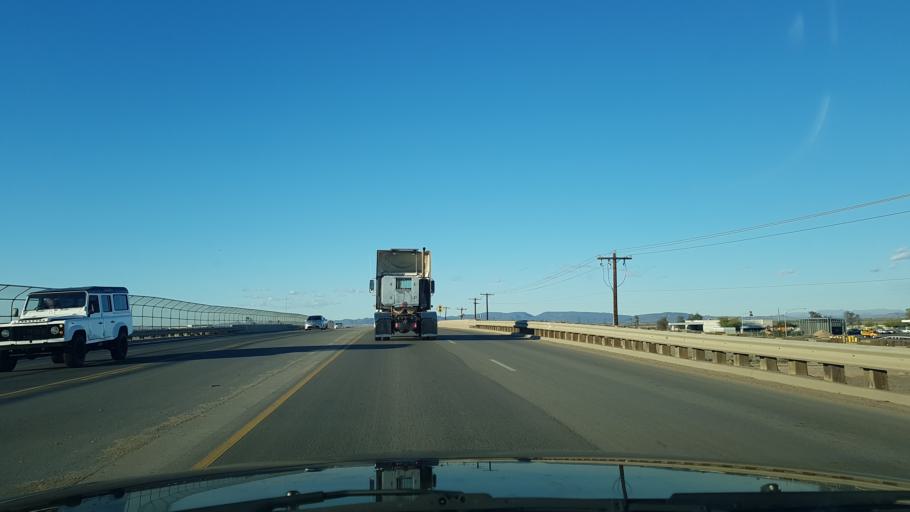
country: US
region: Arizona
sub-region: Yuma County
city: Yuma
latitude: 32.6873
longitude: -114.5988
